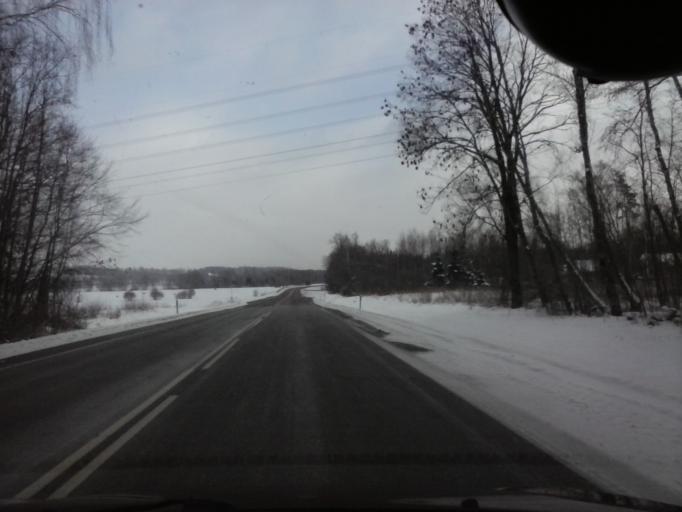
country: EE
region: Viljandimaa
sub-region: Viljandi linn
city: Viljandi
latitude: 58.3529
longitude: 25.4566
